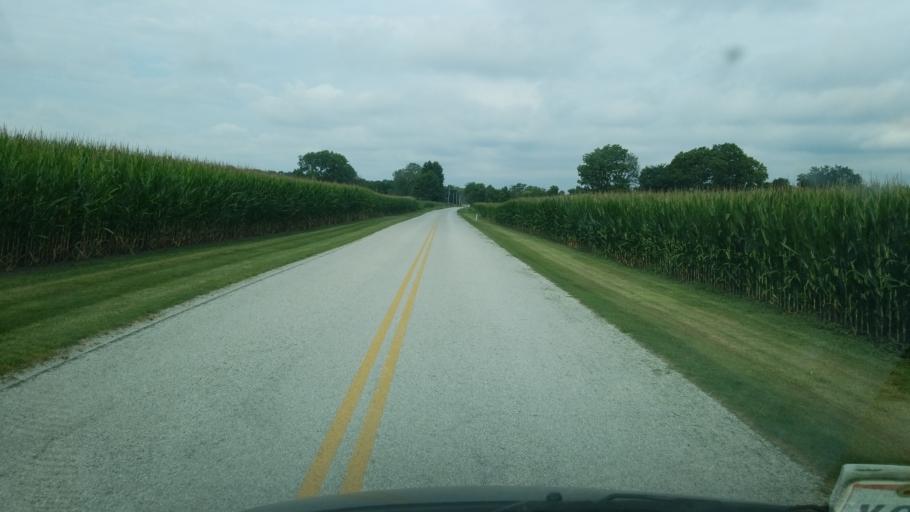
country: US
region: Ohio
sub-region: Sandusky County
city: Green Springs
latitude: 41.1895
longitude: -83.1102
